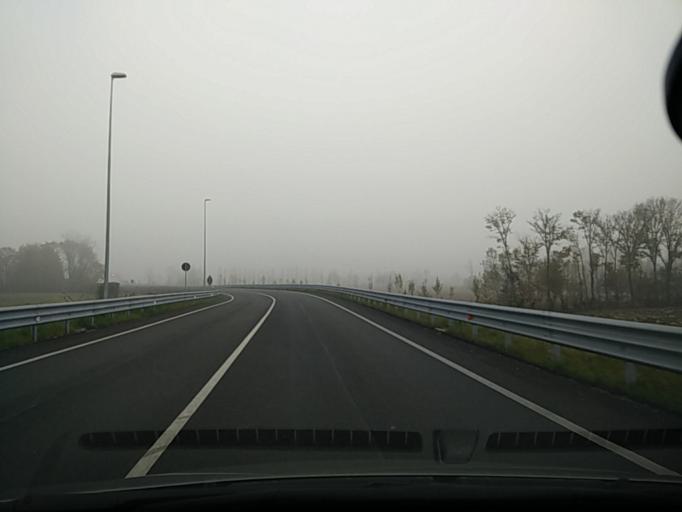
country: IT
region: Veneto
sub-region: Provincia di Venezia
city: Robegano
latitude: 45.5633
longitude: 12.1360
